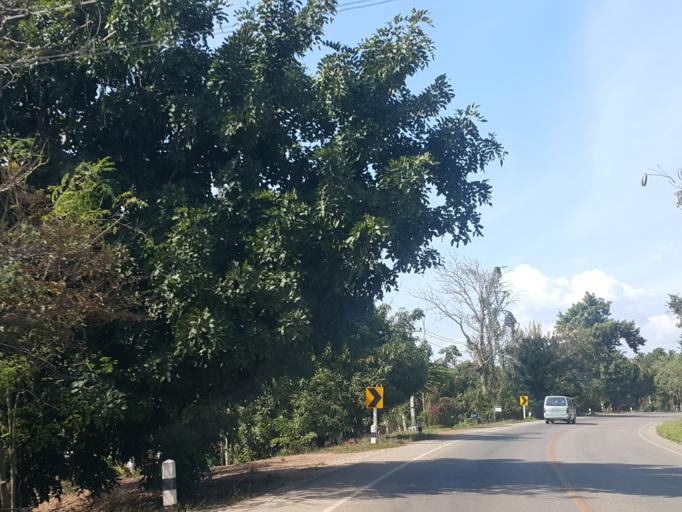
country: TH
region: Sukhothai
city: Sawankhalok
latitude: 17.2685
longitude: 99.8319
